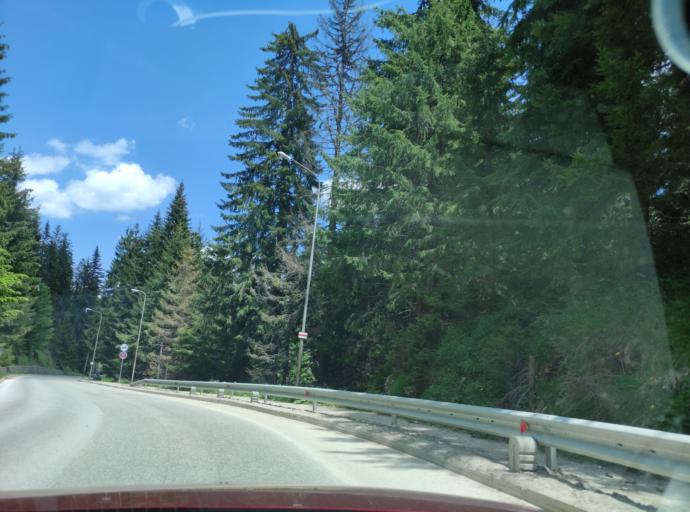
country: BG
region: Smolyan
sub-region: Obshtina Smolyan
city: Smolyan
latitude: 41.6446
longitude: 24.6972
